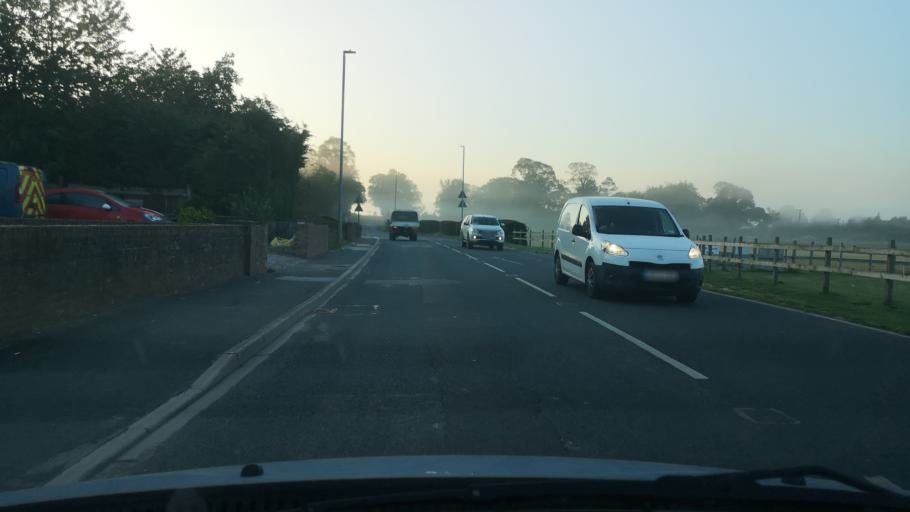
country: GB
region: England
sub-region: East Riding of Yorkshire
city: Goole
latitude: 53.6925
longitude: -0.8658
